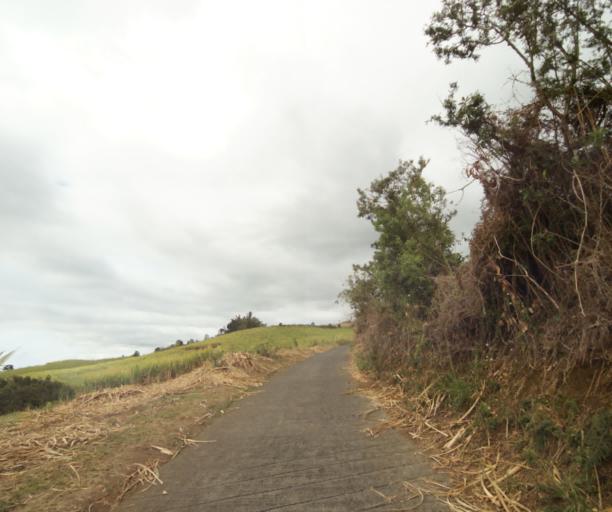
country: RE
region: Reunion
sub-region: Reunion
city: Saint-Paul
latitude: -21.0263
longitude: 55.3203
